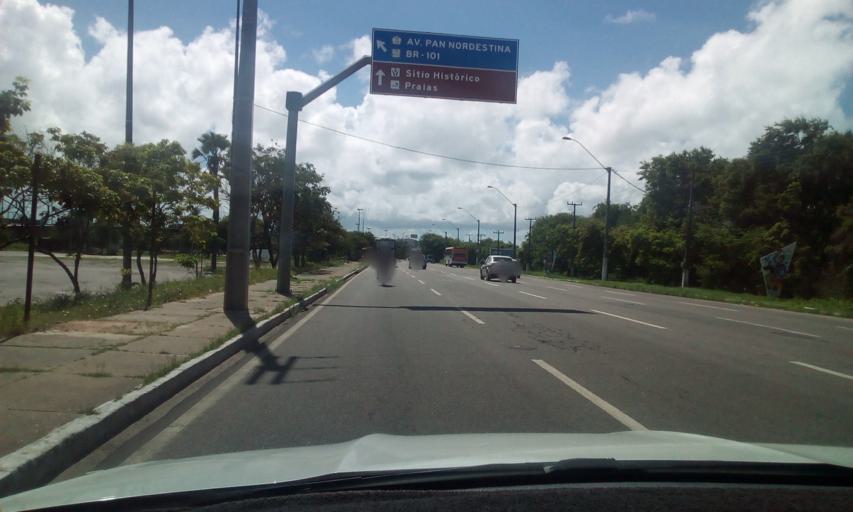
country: BR
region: Pernambuco
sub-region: Olinda
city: Olinda
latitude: -8.0313
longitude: -34.8655
